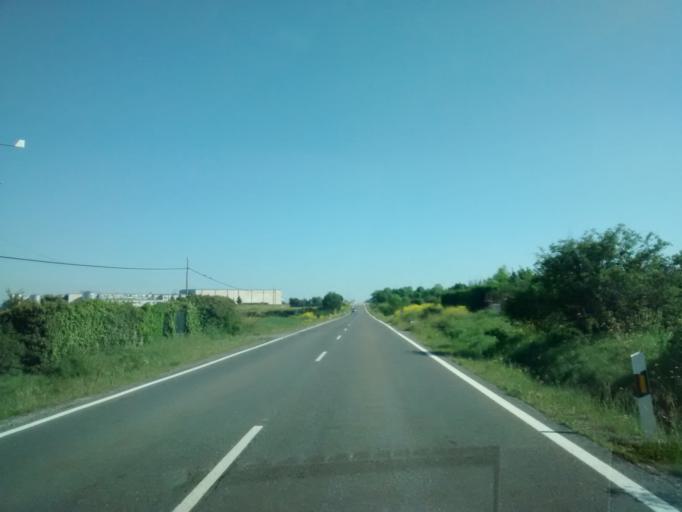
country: ES
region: Castille and Leon
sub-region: Provincia de Segovia
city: Trescasas
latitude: 40.9460
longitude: -4.0340
